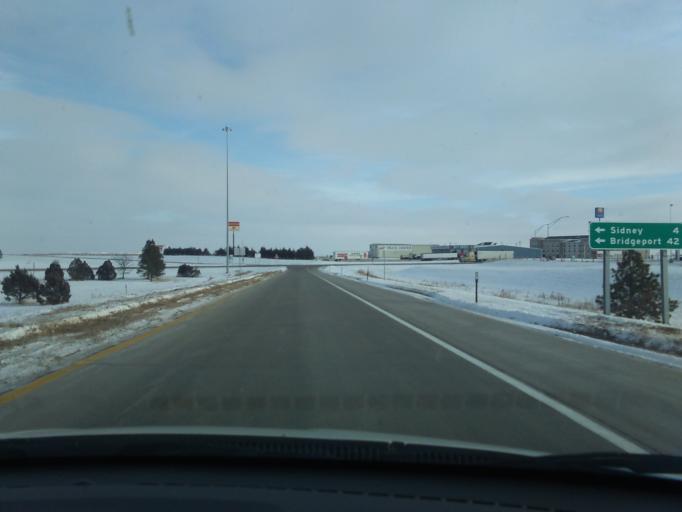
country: US
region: Nebraska
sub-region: Cheyenne County
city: Sidney
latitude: 41.1122
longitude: -102.9513
